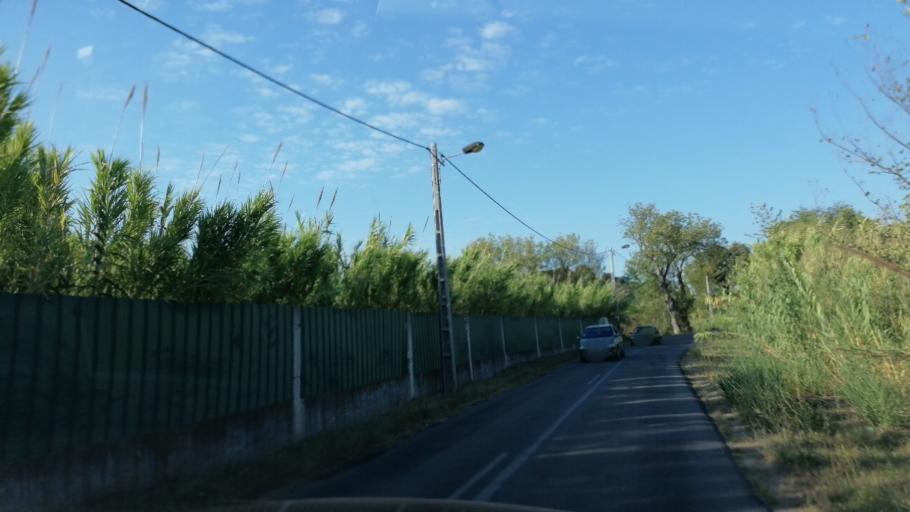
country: PT
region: Santarem
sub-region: Santarem
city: Santarem
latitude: 39.2585
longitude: -8.6691
